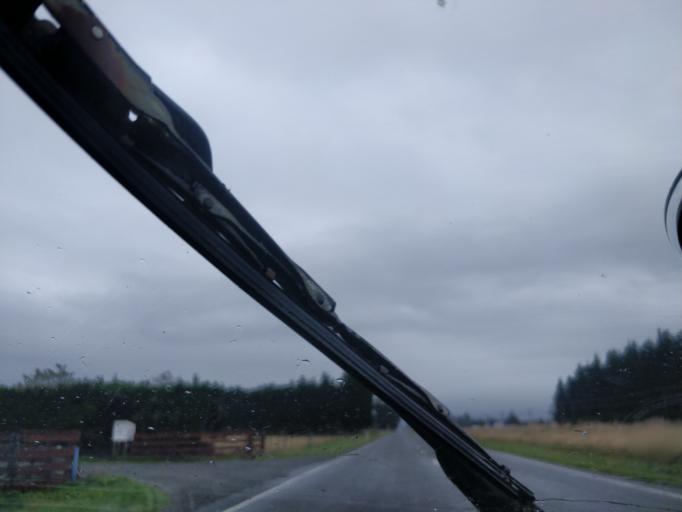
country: NZ
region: Canterbury
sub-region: Selwyn District
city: Darfield
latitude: -43.3798
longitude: 172.0036
